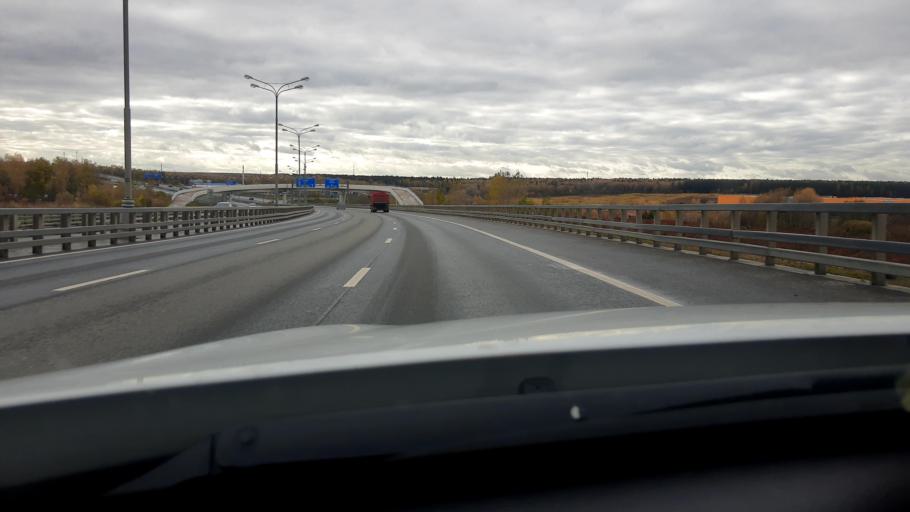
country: RU
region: Moscow
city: Vnukovo
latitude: 55.5822
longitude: 37.2082
